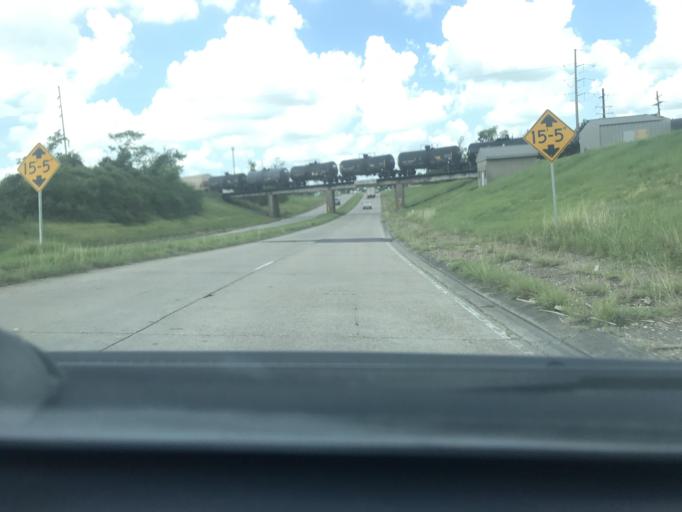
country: US
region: Louisiana
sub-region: Calcasieu Parish
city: Westlake
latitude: 30.2374
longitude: -93.2820
